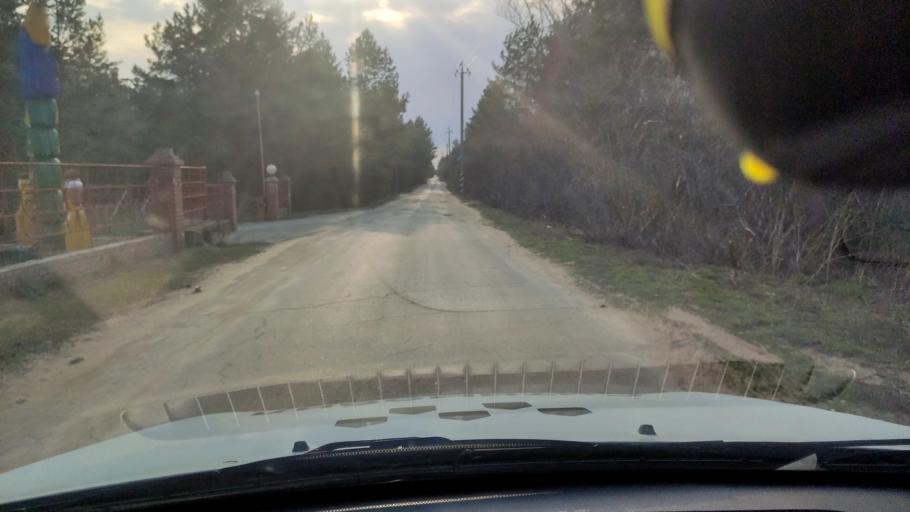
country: RU
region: Samara
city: Zhigulevsk
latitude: 53.4588
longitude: 49.6242
